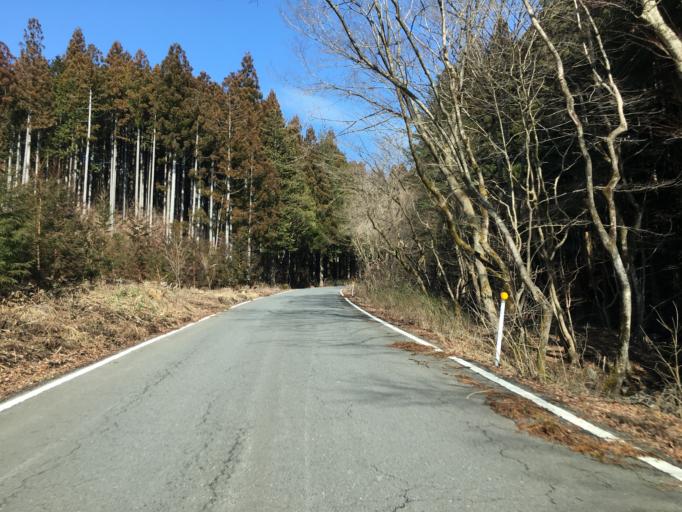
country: JP
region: Ibaraki
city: Takahagi
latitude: 36.8304
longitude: 140.5522
